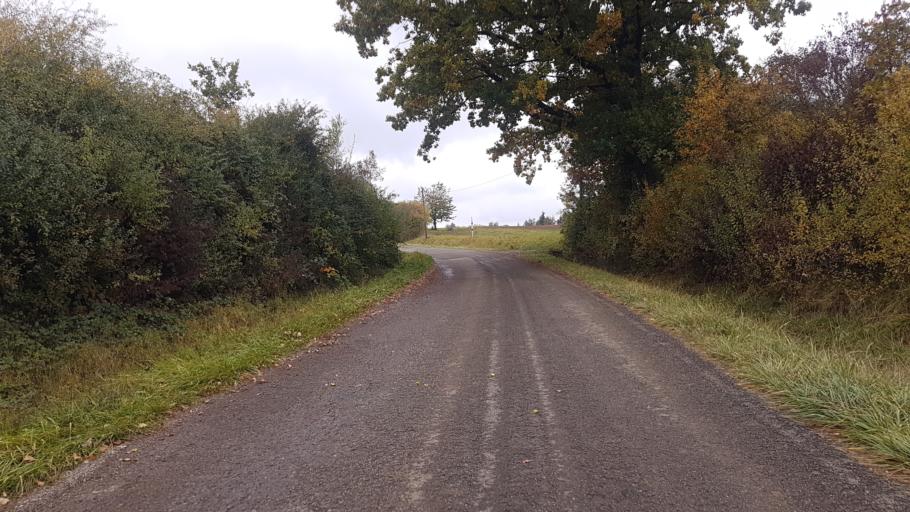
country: DE
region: Baden-Wuerttemberg
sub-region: Tuebingen Region
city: Dusslingen
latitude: 48.4601
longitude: 9.0473
